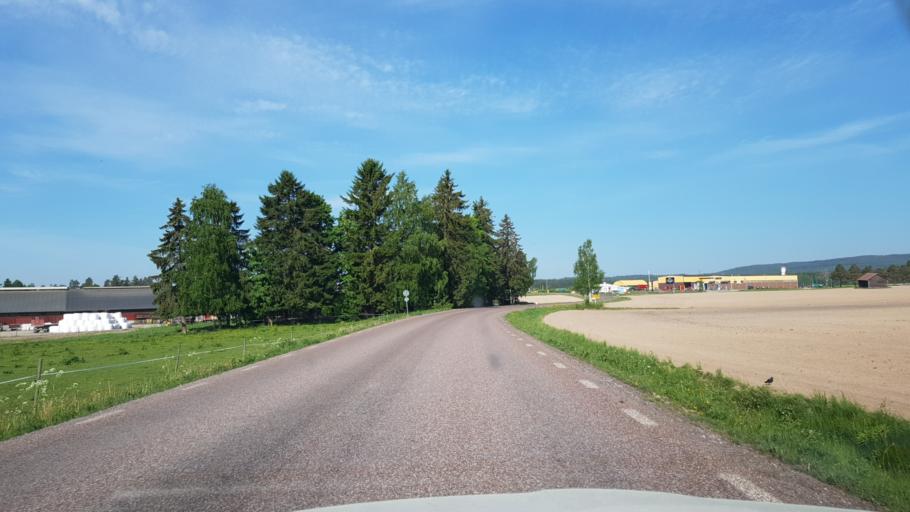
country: SE
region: Dalarna
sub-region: Saters Kommun
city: Saeter
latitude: 60.4165
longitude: 15.7537
